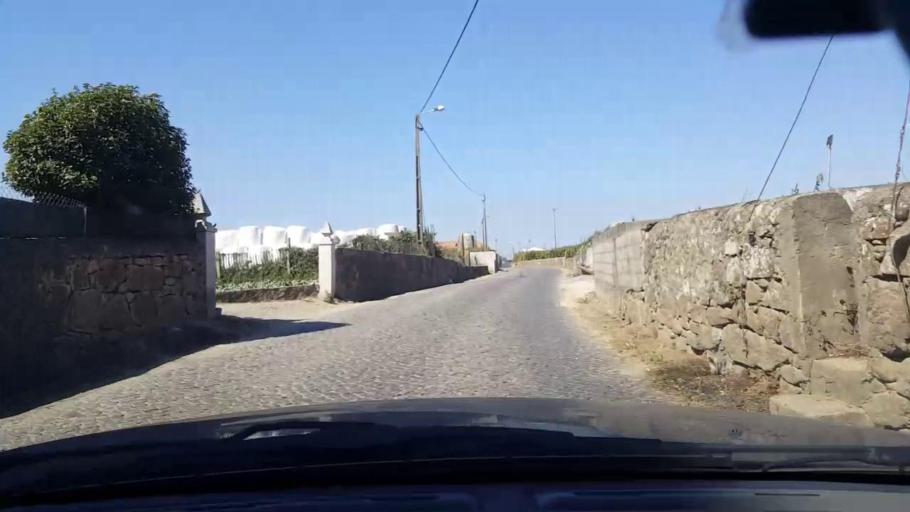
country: PT
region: Porto
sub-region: Matosinhos
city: Lavra
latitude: 41.2771
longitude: -8.7112
